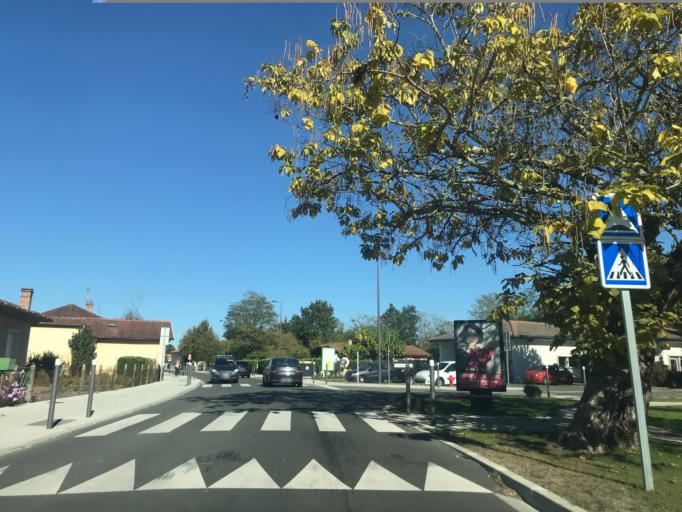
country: FR
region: Aquitaine
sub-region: Departement de la Gironde
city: Marcheprime
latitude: 44.6526
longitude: -0.8541
